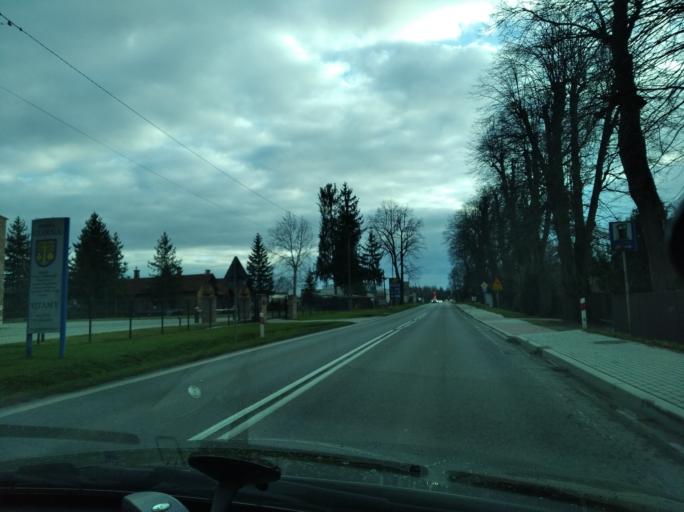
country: PL
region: Subcarpathian Voivodeship
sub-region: Powiat lancucki
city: Rakszawa
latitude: 50.1242
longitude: 22.2316
